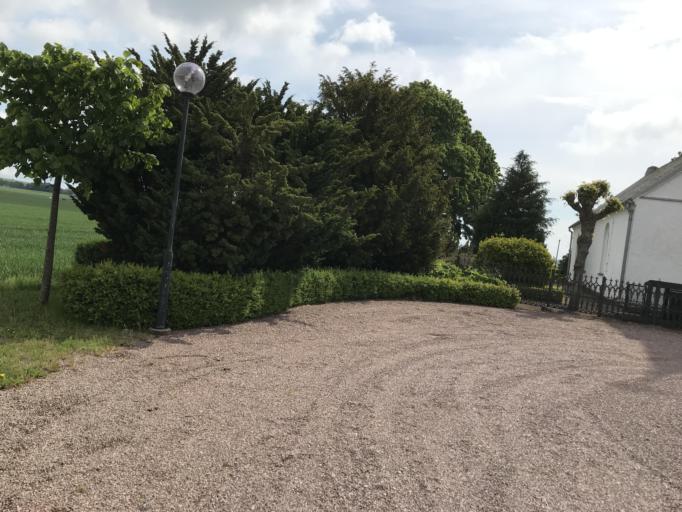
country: SE
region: Skane
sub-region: Landskrona
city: Landskrona
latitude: 55.9049
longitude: 12.8543
